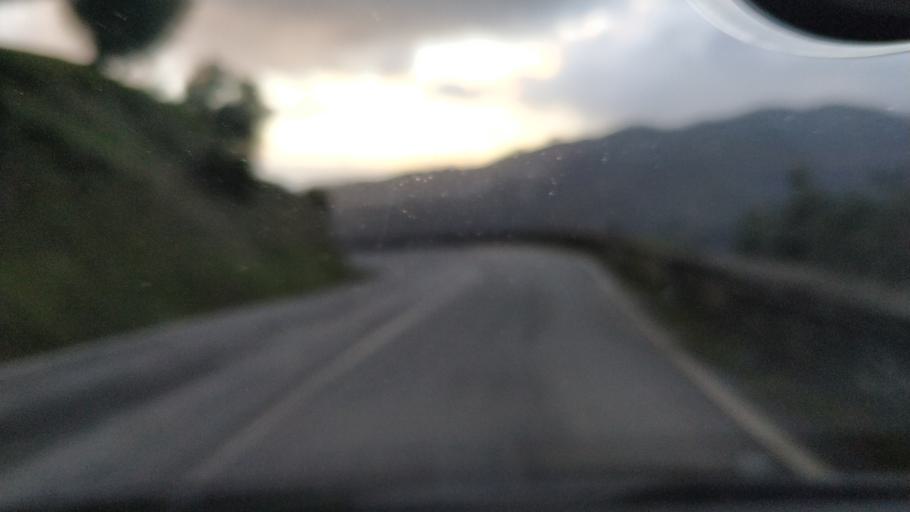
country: PT
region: Vila Real
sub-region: Santa Marta de Penaguiao
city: Santa Marta de Penaguiao
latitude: 41.2461
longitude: -7.7683
